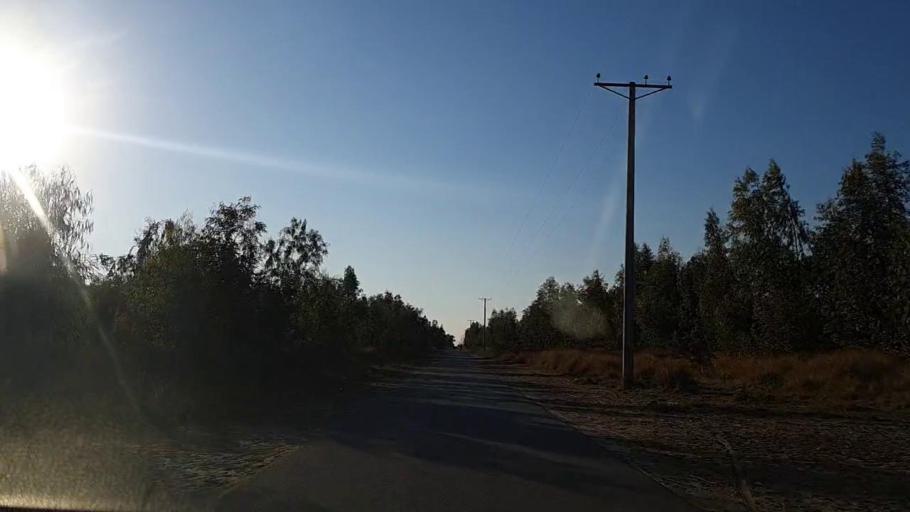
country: PK
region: Sindh
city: Khadro
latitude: 26.2790
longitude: 68.9010
